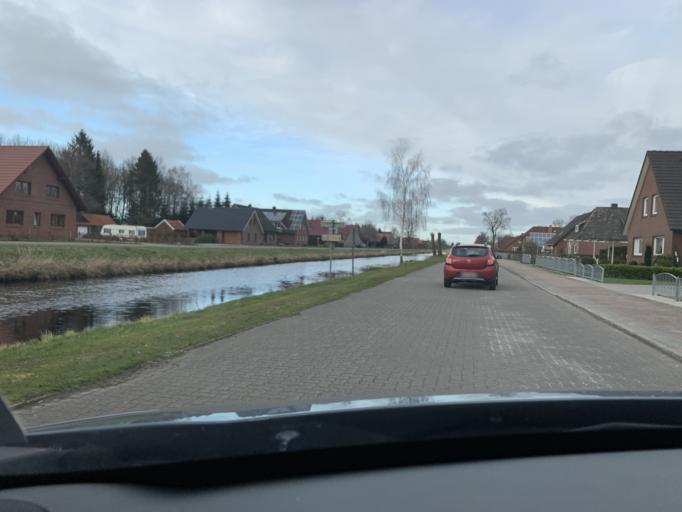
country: DE
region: Lower Saxony
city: Schwerinsdorf
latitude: 53.2716
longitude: 7.6974
